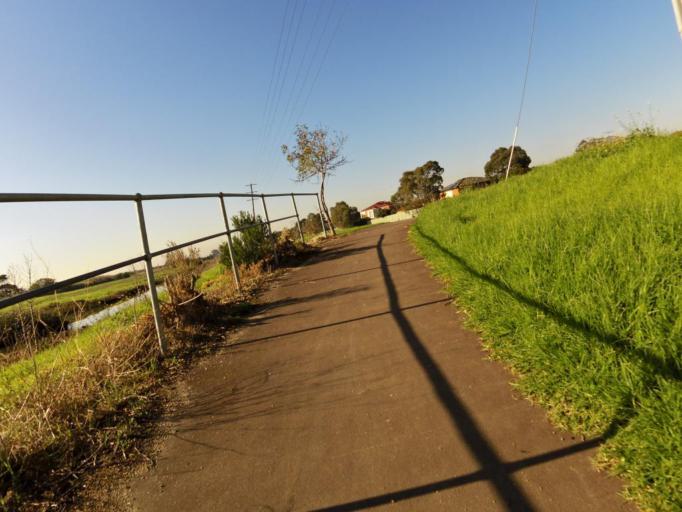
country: AU
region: Victoria
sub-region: Kingston
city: Aspendale
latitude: -38.0122
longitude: 145.1037
